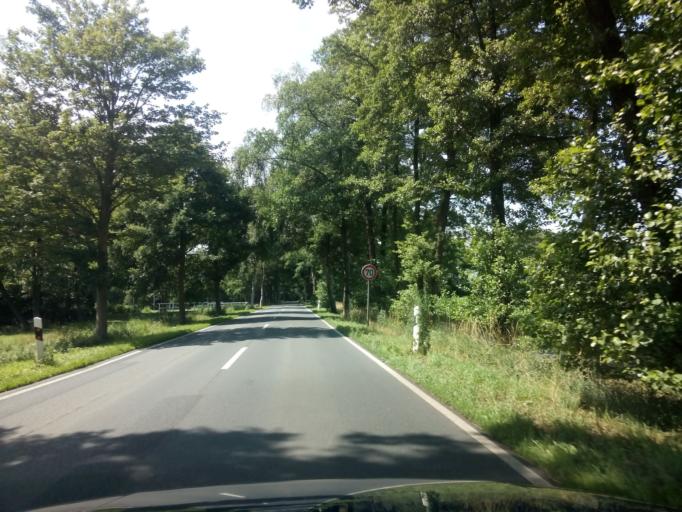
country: DE
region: Lower Saxony
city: Worpswede
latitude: 53.2574
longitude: 8.9483
